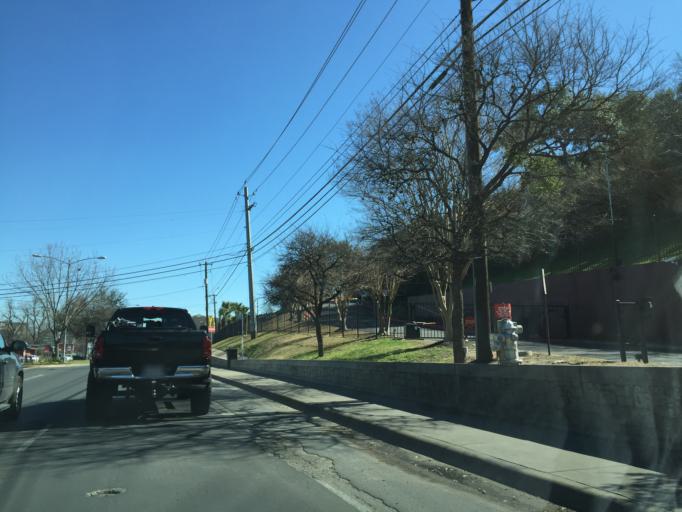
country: US
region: Texas
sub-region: Travis County
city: Austin
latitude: 30.2616
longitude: -97.7605
